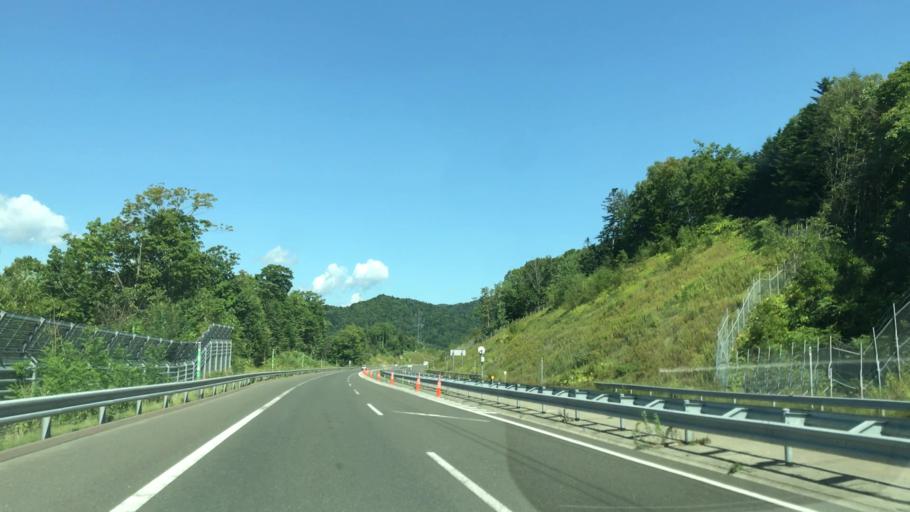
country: JP
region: Hokkaido
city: Shimo-furano
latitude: 42.9948
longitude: 142.4098
